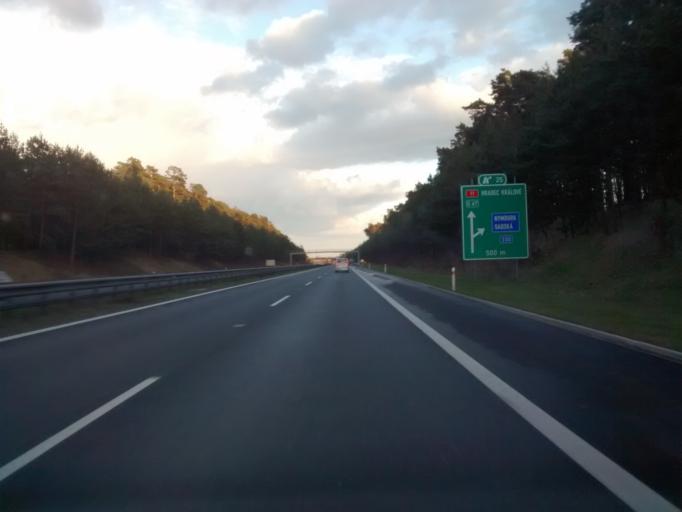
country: CZ
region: Central Bohemia
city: Poricany
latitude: 50.1221
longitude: 14.9320
